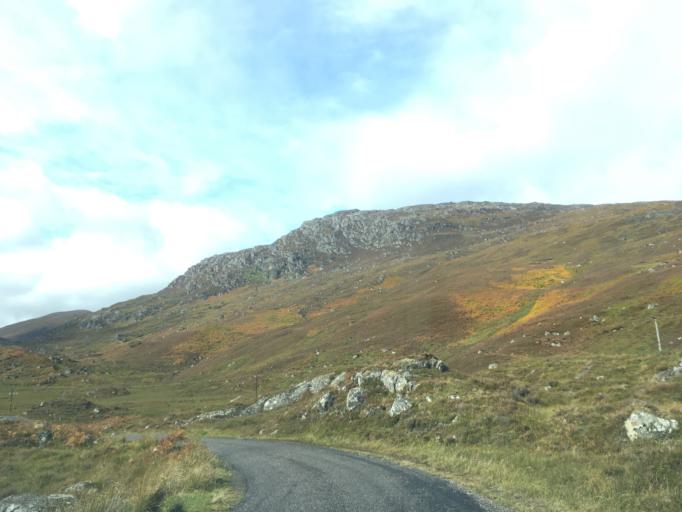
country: GB
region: Scotland
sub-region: Highland
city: Spean Bridge
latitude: 57.3409
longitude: -4.9491
